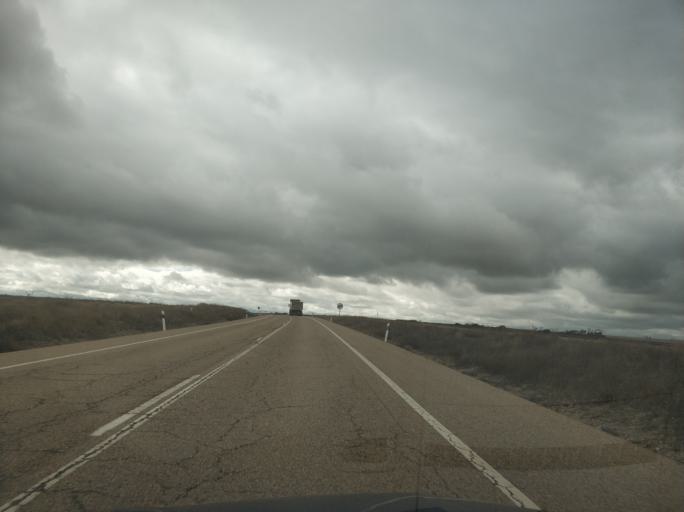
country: ES
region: Castille and Leon
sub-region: Provincia de Zamora
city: Castrillo de la Guarena
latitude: 41.2507
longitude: -5.2874
